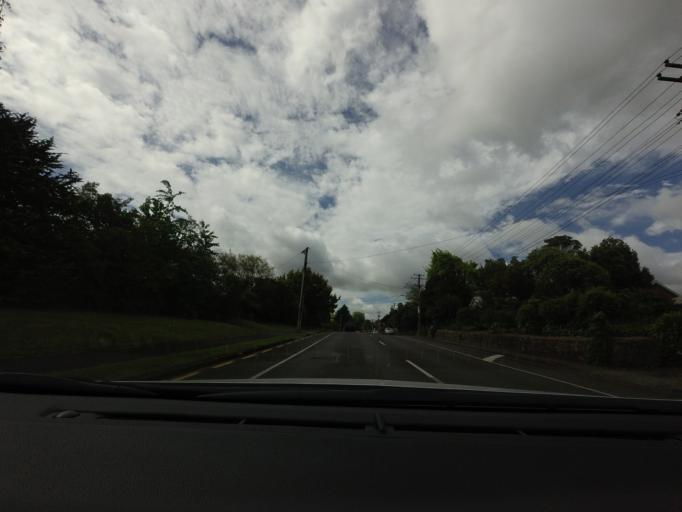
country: NZ
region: Bay of Plenty
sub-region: Rotorua District
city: Rotorua
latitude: -38.1547
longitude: 176.2409
